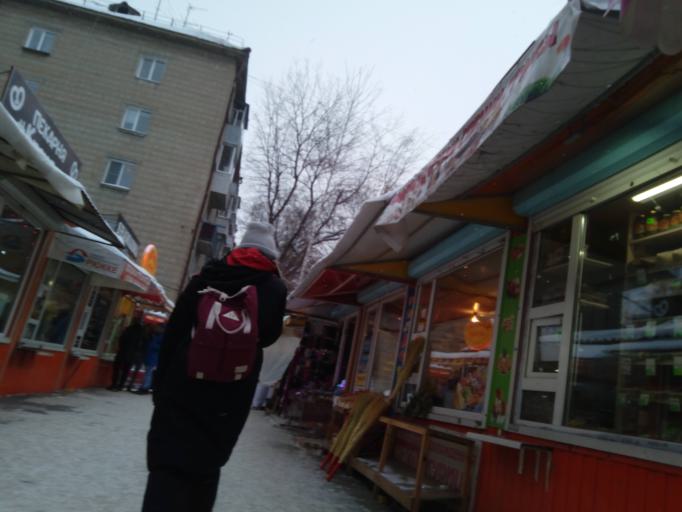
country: RU
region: Novosibirsk
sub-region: Novosibirskiy Rayon
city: Novosibirsk
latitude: 54.9897
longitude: 82.9044
